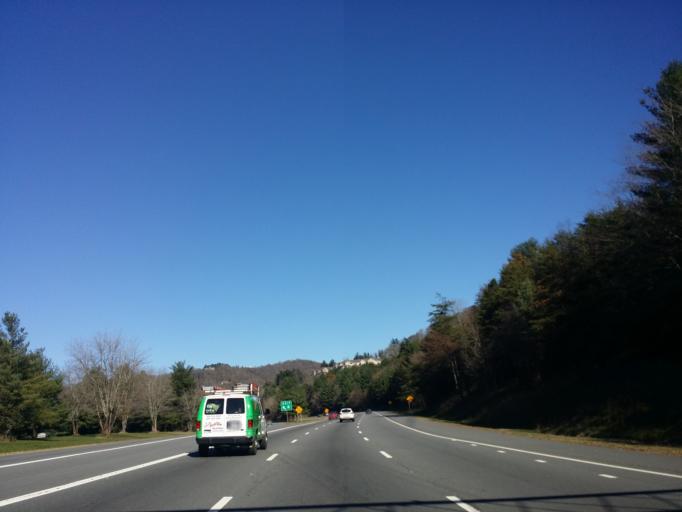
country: US
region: North Carolina
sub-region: Buncombe County
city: Asheville
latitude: 35.5917
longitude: -82.5275
